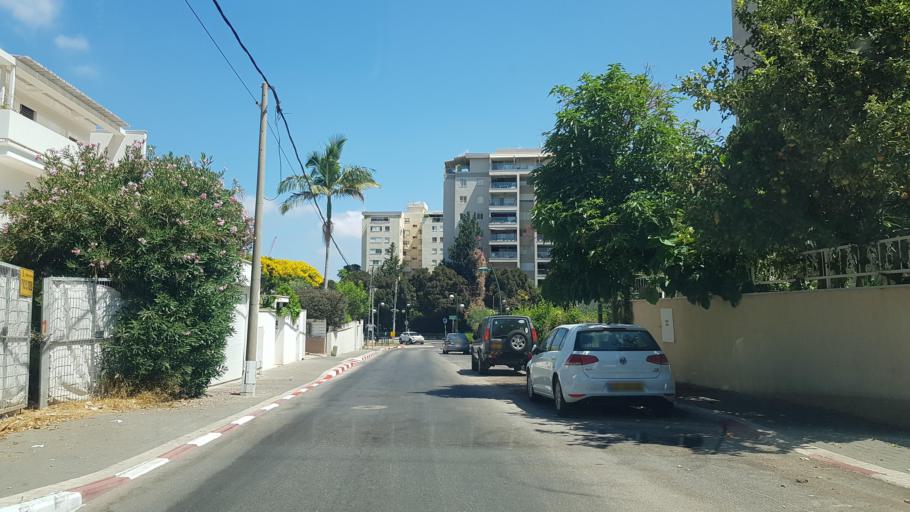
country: IL
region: Tel Aviv
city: Ramat HaSharon
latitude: 32.1517
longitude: 34.8395
